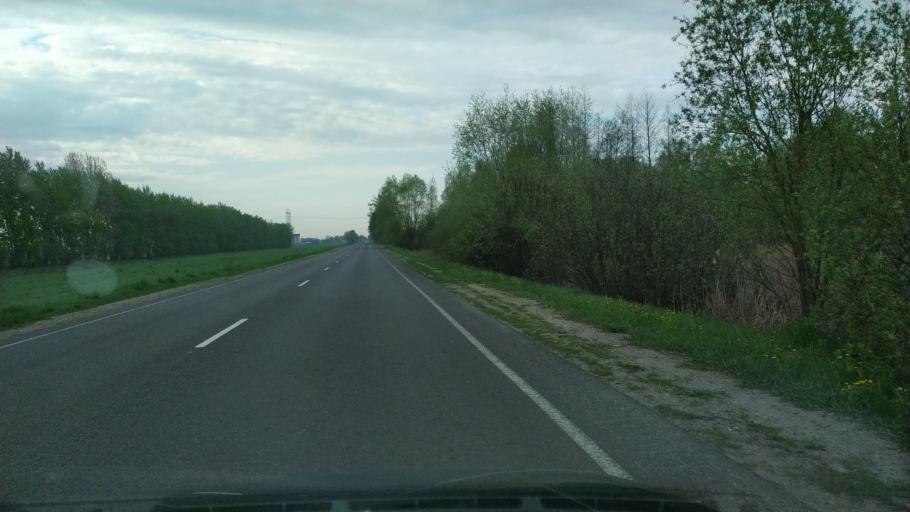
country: BY
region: Brest
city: Zhabinka
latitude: 52.2174
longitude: 23.9952
